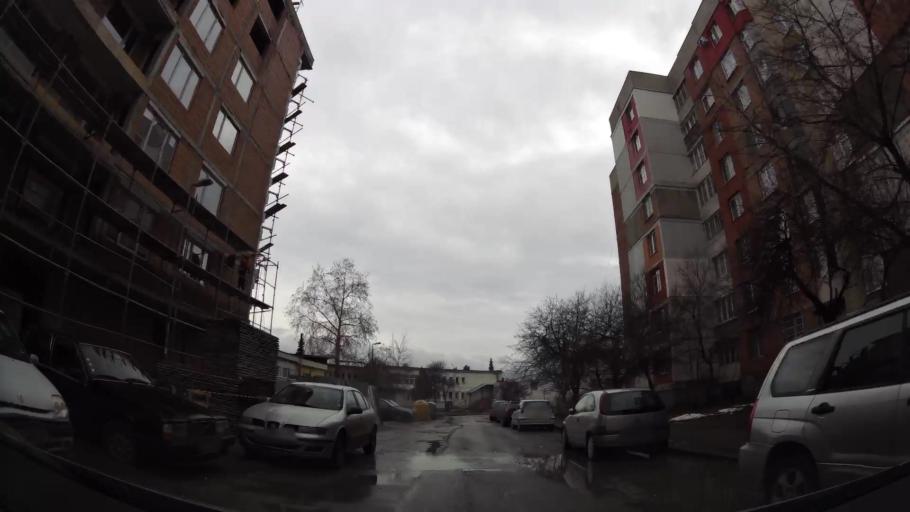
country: BG
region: Sofiya
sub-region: Obshtina Bozhurishte
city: Bozhurishte
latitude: 42.7283
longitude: 23.2559
